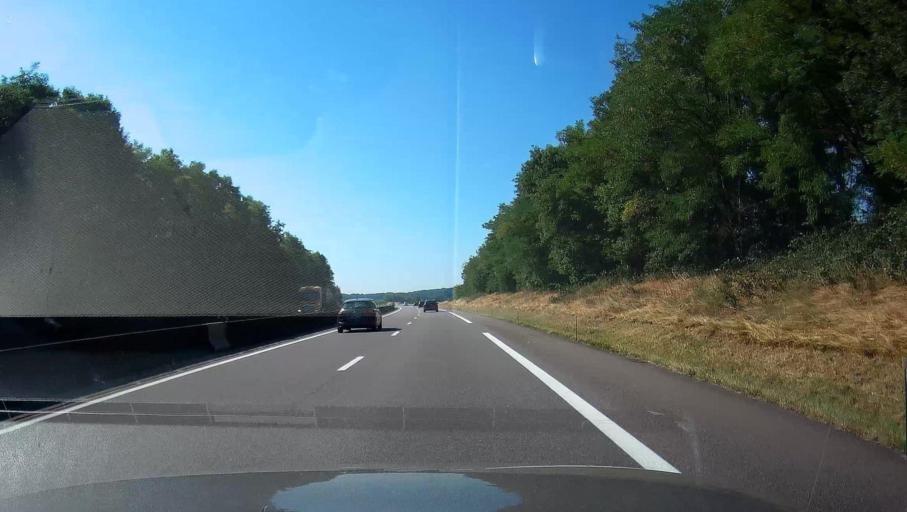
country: FR
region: Lorraine
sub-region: Departement des Vosges
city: Chatenois
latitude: 48.3903
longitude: 5.8797
